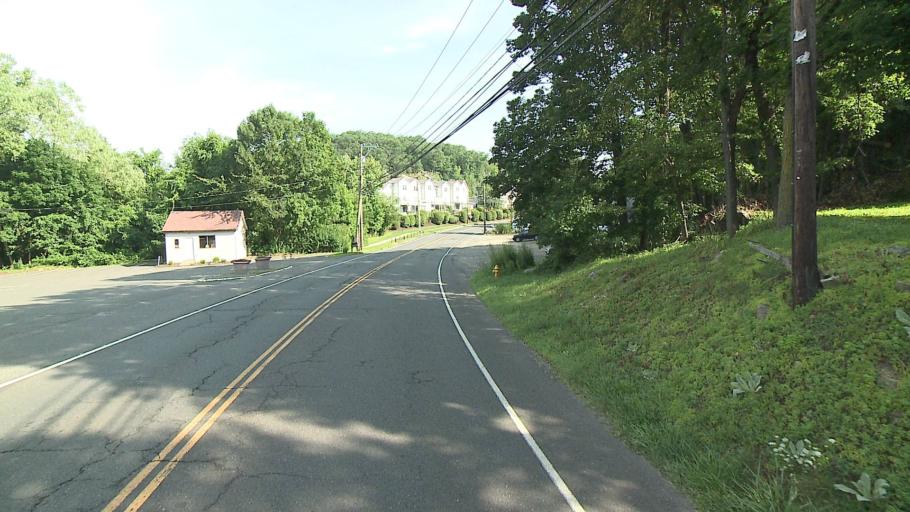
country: US
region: Connecticut
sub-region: Fairfield County
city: Danbury
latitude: 41.4252
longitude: -73.4730
